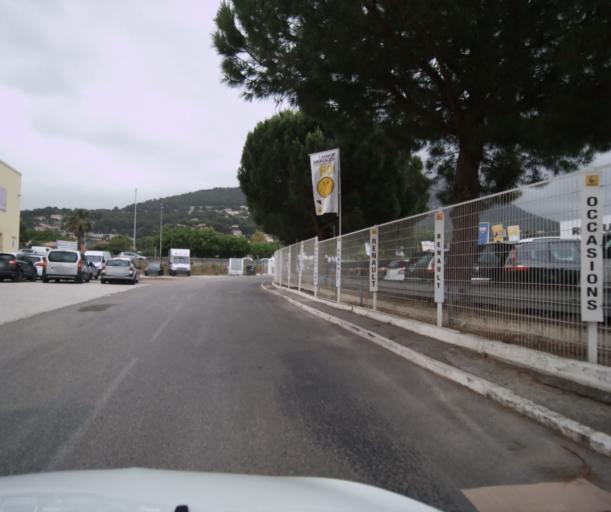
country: FR
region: Provence-Alpes-Cote d'Azur
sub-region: Departement du Var
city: La Valette-du-Var
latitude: 43.1395
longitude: 5.9991
